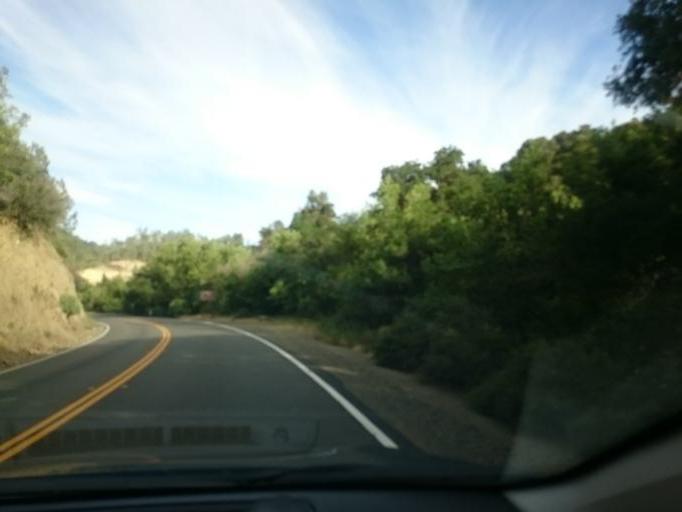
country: US
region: California
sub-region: Napa County
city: Yountville
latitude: 38.4976
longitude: -122.2546
